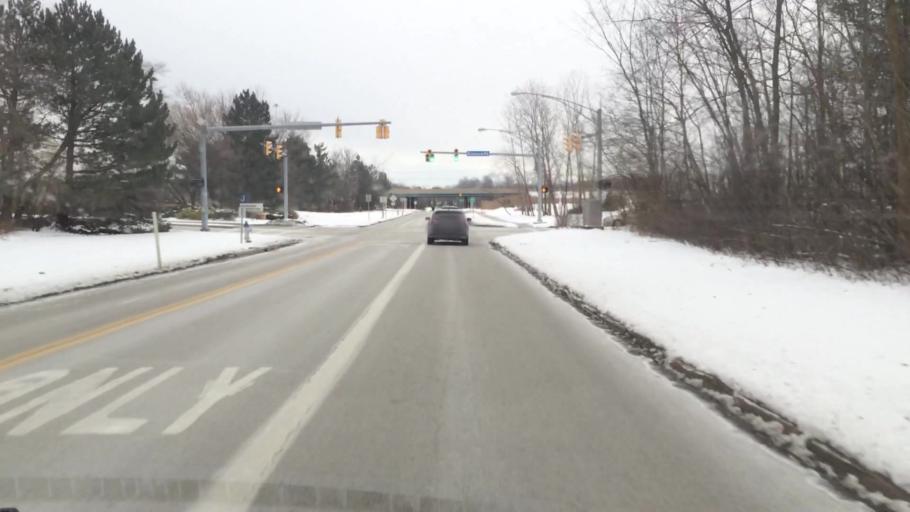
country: US
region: Ohio
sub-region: Cuyahoga County
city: Beachwood
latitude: 41.4736
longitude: -81.4921
